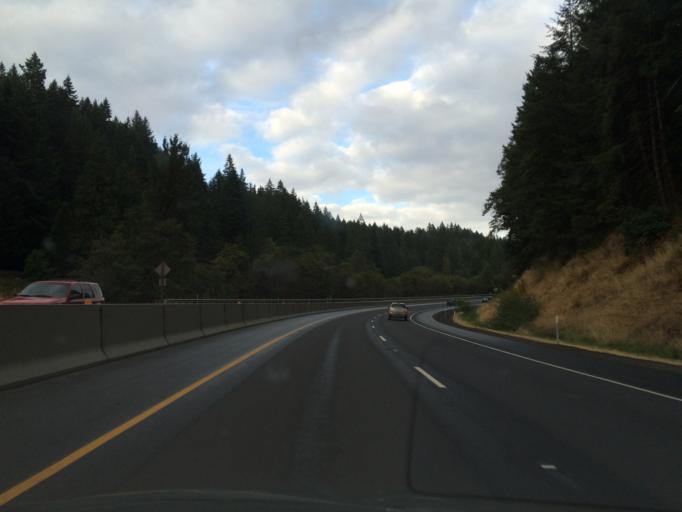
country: US
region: Oregon
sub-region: Lane County
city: Cottage Grove
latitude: 43.7530
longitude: -123.1417
